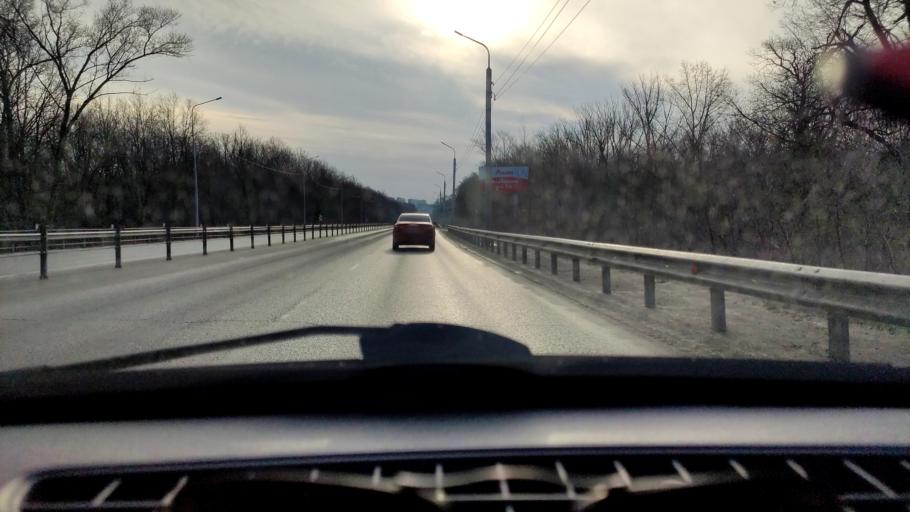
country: RU
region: Bashkortostan
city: Ufa
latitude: 54.7000
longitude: 55.9208
